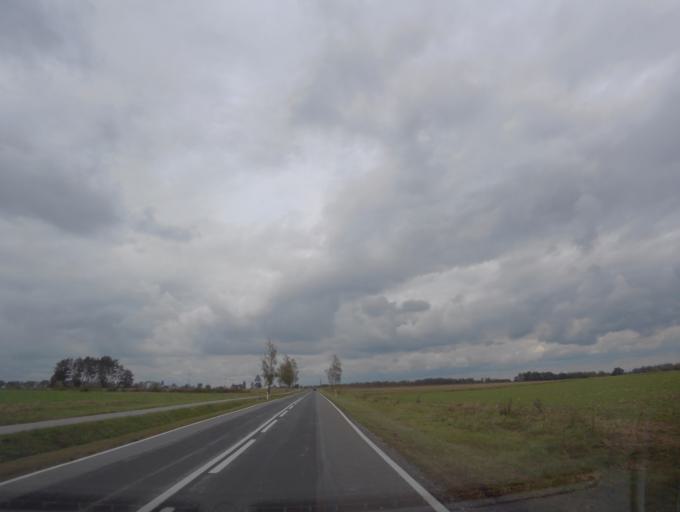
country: PL
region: Lublin Voivodeship
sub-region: Powiat wlodawski
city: Wlodawa
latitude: 51.6412
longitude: 23.5233
